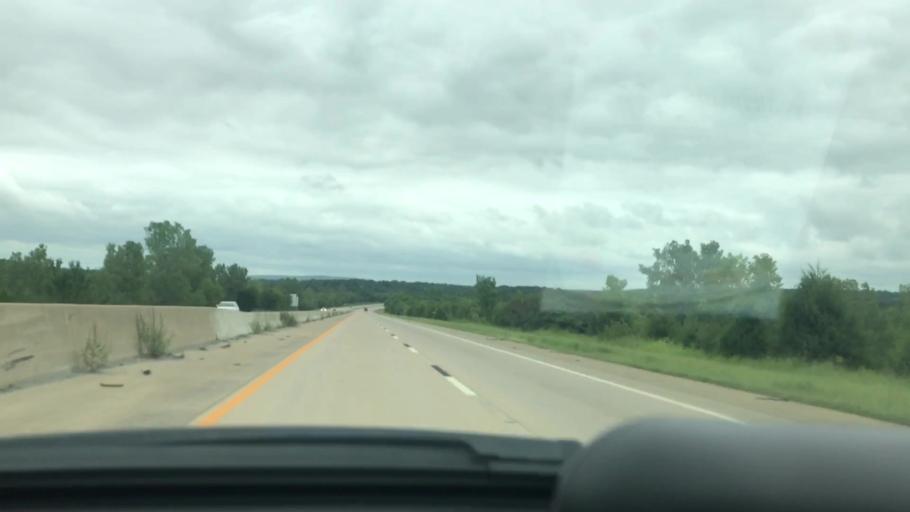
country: US
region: Oklahoma
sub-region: McIntosh County
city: Eufaula
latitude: 35.1862
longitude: -95.6408
